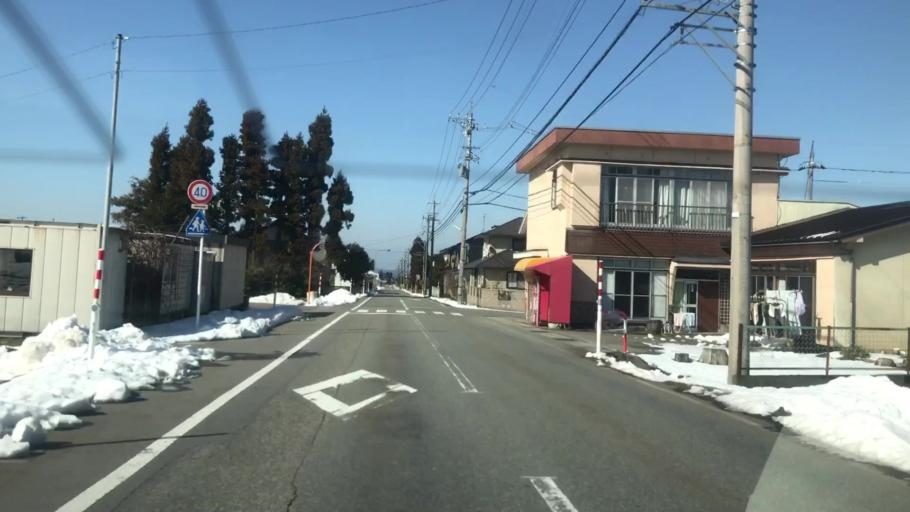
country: JP
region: Toyama
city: Toyama-shi
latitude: 36.6237
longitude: 137.2803
